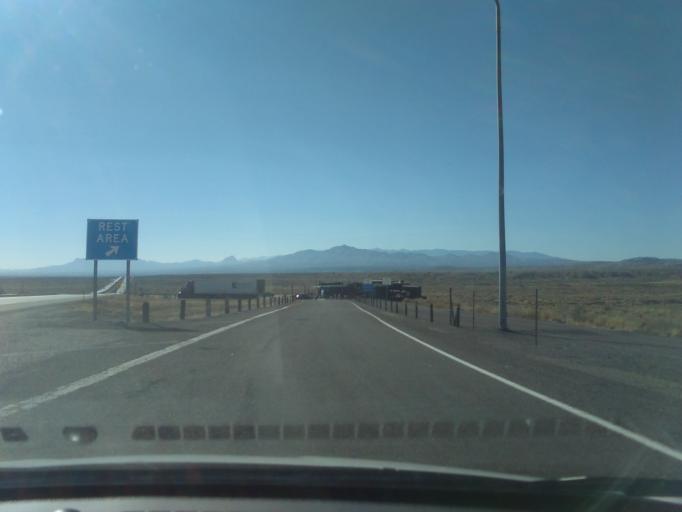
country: US
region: New Mexico
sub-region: Socorro County
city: Socorro
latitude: 34.3069
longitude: -106.8894
